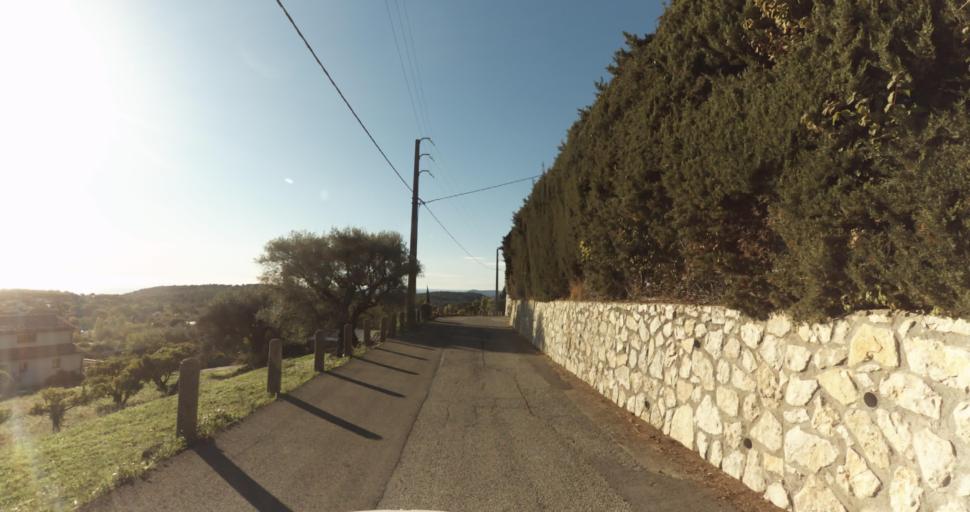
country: FR
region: Provence-Alpes-Cote d'Azur
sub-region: Departement des Alpes-Maritimes
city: Vence
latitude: 43.7281
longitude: 7.0851
